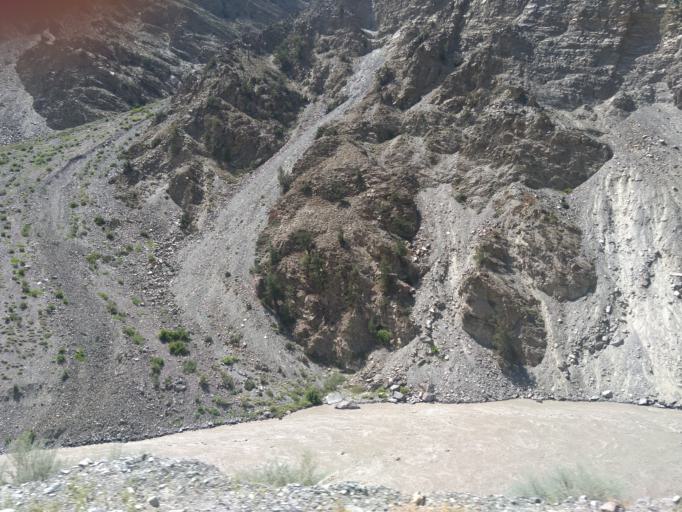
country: CN
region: Tibet Autonomous Region
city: Diyag
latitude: 31.6880
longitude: 78.5049
